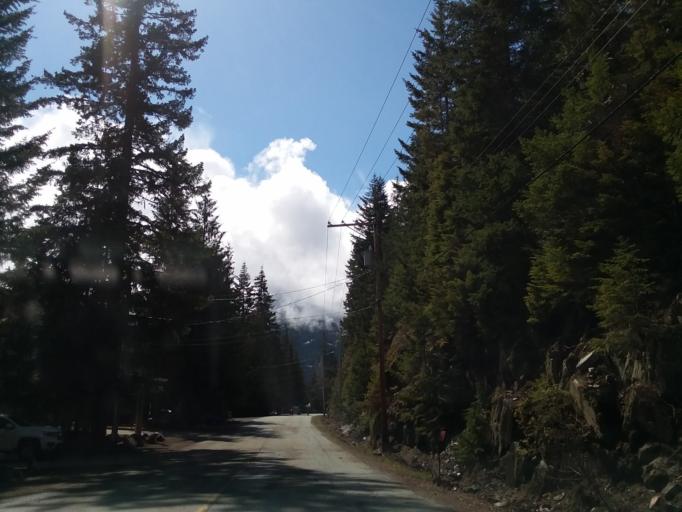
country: CA
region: British Columbia
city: Whistler
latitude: 50.1139
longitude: -122.9862
